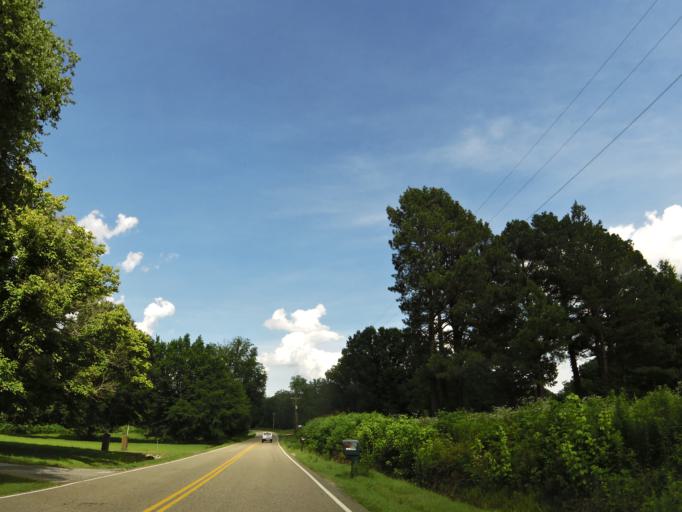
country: US
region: Tennessee
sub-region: Gibson County
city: Milan
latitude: 35.9752
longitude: -88.7453
